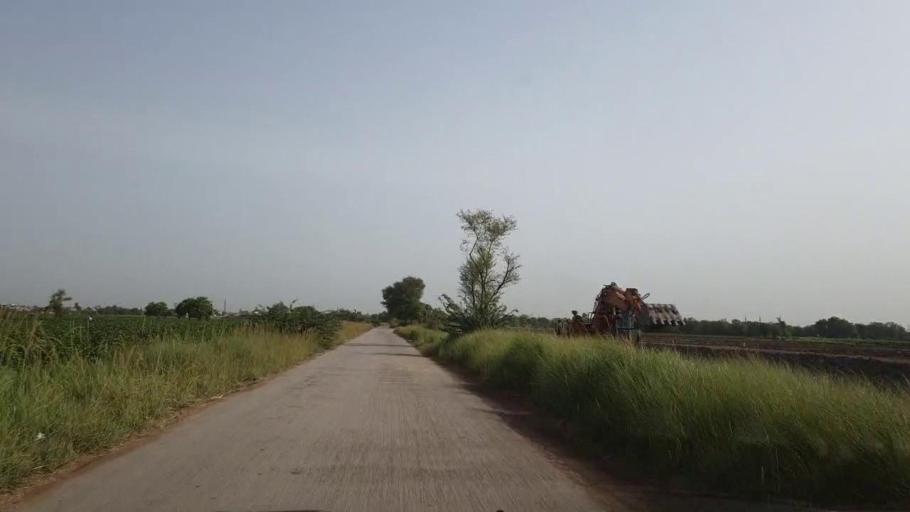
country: PK
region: Sindh
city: Nawabshah
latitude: 26.2260
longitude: 68.4053
